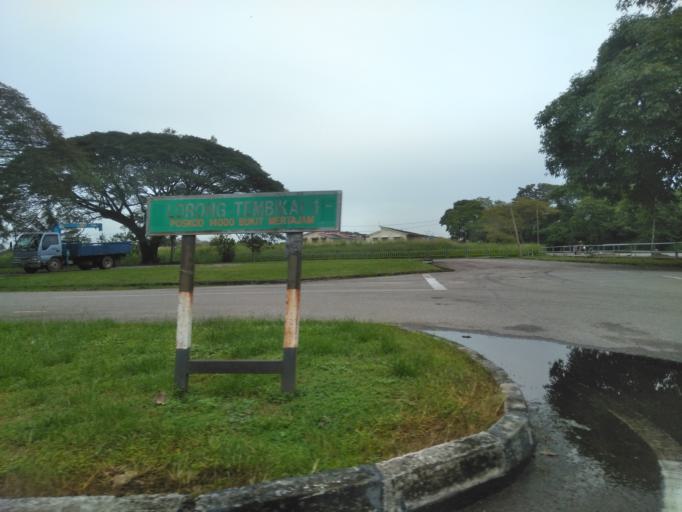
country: MY
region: Penang
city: Bukit Mertajam
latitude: 5.3585
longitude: 100.4499
